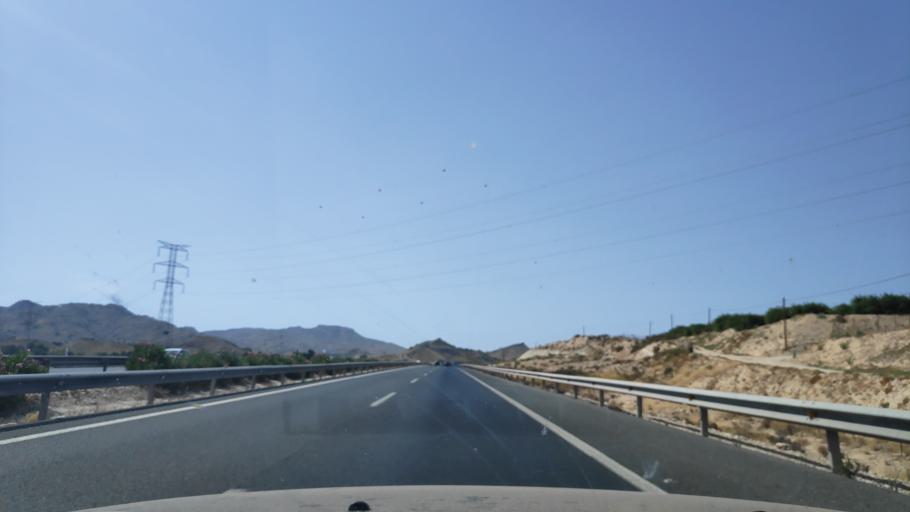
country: ES
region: Murcia
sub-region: Murcia
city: Archena
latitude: 38.1472
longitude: -1.2771
